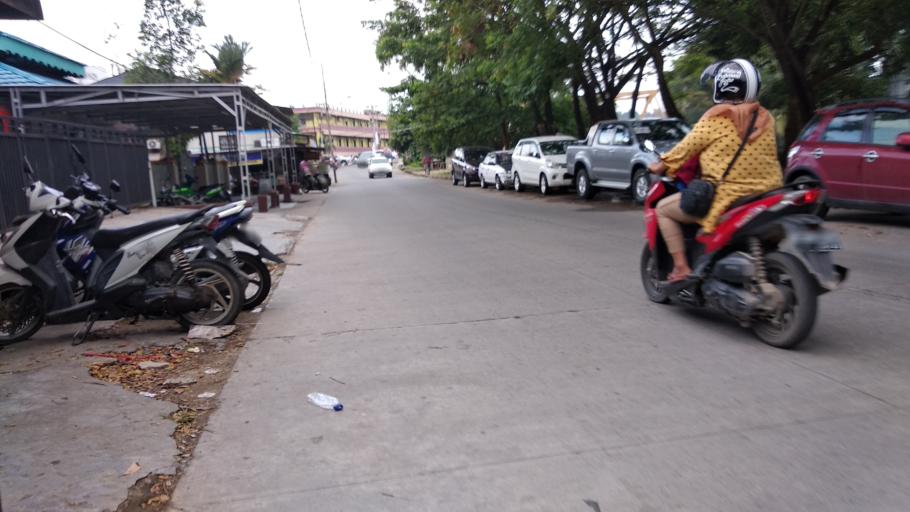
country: ID
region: East Kalimantan
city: Samarinda
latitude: -0.4917
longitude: 117.1533
